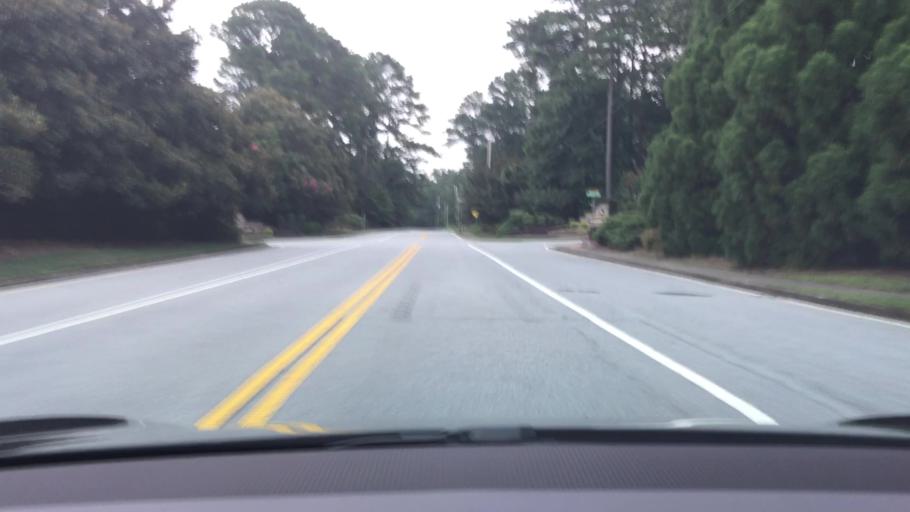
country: US
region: Georgia
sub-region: Gwinnett County
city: Suwanee
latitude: 34.0789
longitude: -84.0817
